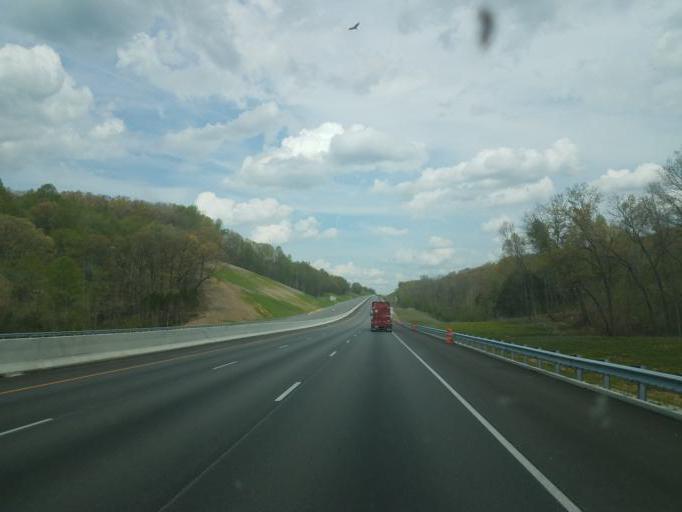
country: US
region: Kentucky
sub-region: Hart County
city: Munfordville
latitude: 37.3092
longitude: -85.9035
